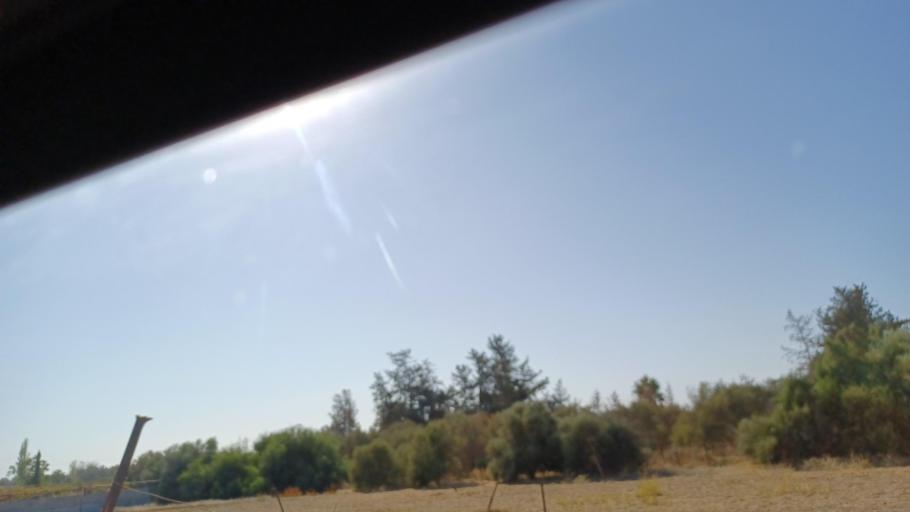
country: CY
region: Larnaka
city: Kolossi
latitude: 34.6679
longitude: 32.9500
